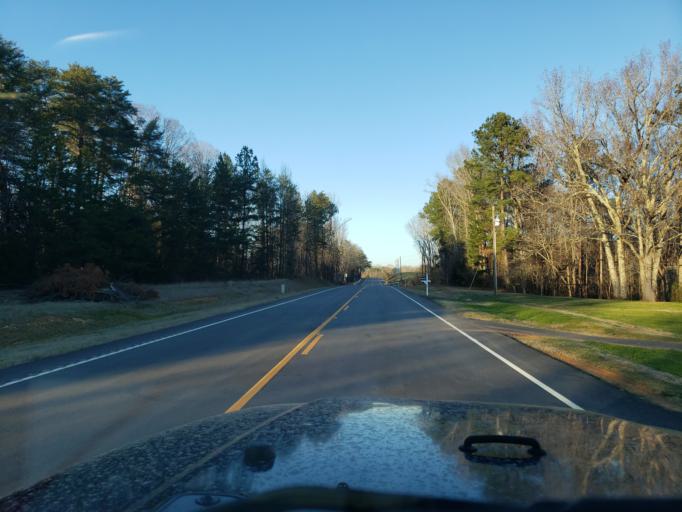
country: US
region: South Carolina
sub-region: Cherokee County
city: Blacksburg
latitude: 35.0212
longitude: -81.4048
